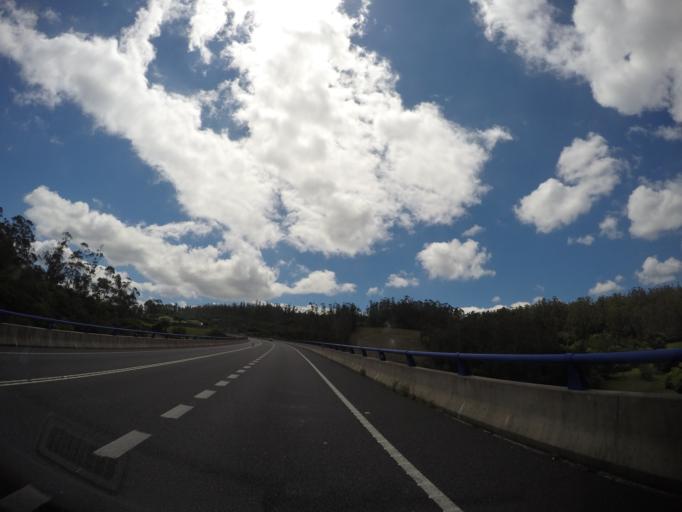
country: ES
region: Aragon
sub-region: Provincia de Zaragoza
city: El Burgo de Ebro
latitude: 41.5783
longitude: -0.8072
